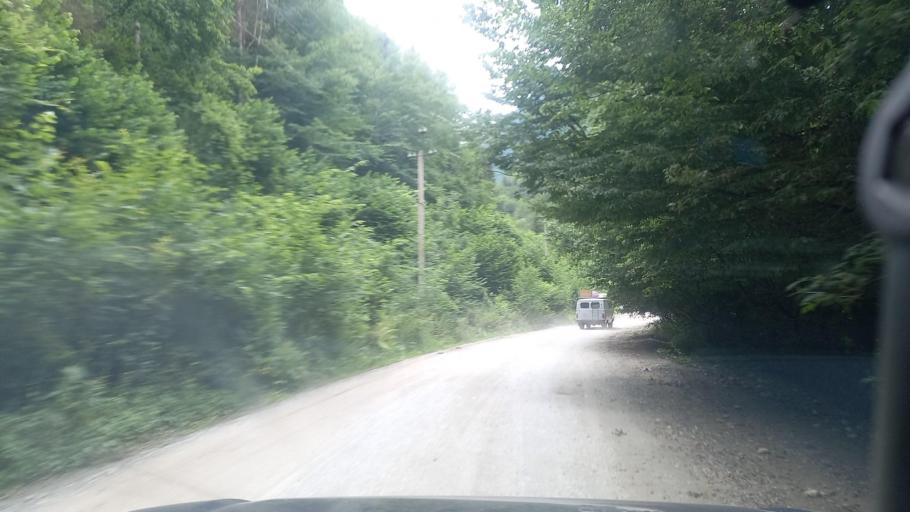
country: RU
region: Karachayevo-Cherkesiya
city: Kurdzhinovo
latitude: 43.8099
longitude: 40.9126
